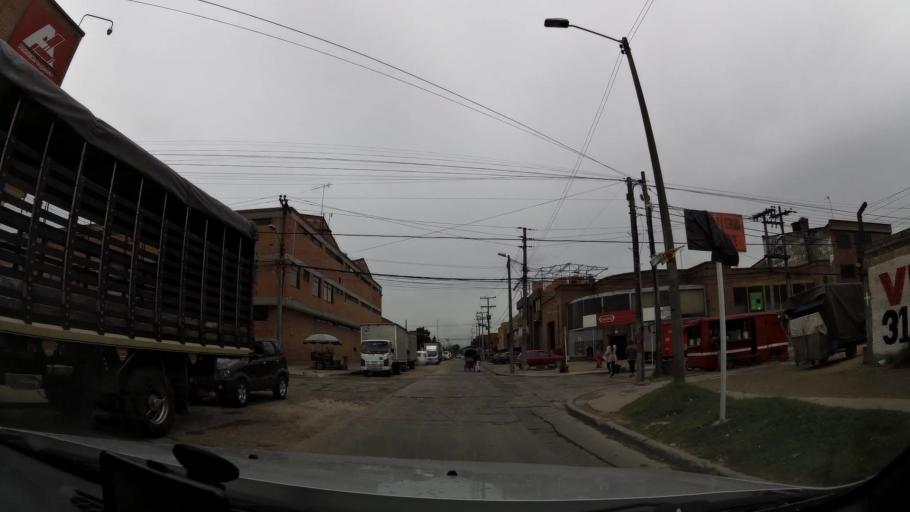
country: CO
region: Bogota D.C.
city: Bogota
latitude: 4.6461
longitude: -74.1222
